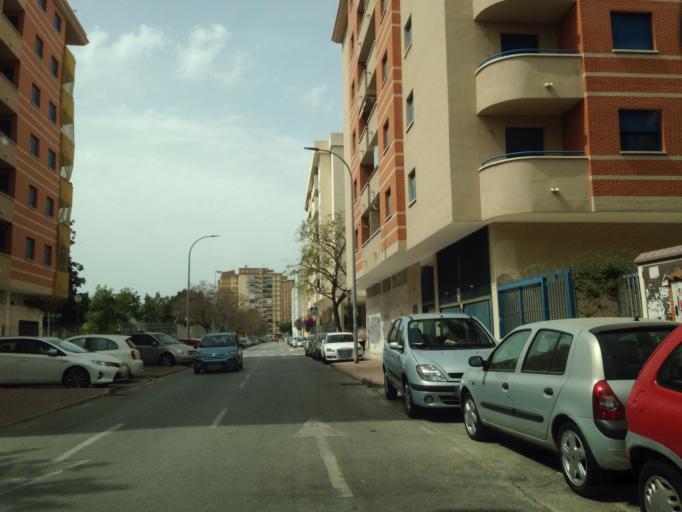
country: ES
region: Andalusia
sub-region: Provincia de Malaga
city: Malaga
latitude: 36.7081
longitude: -4.4319
